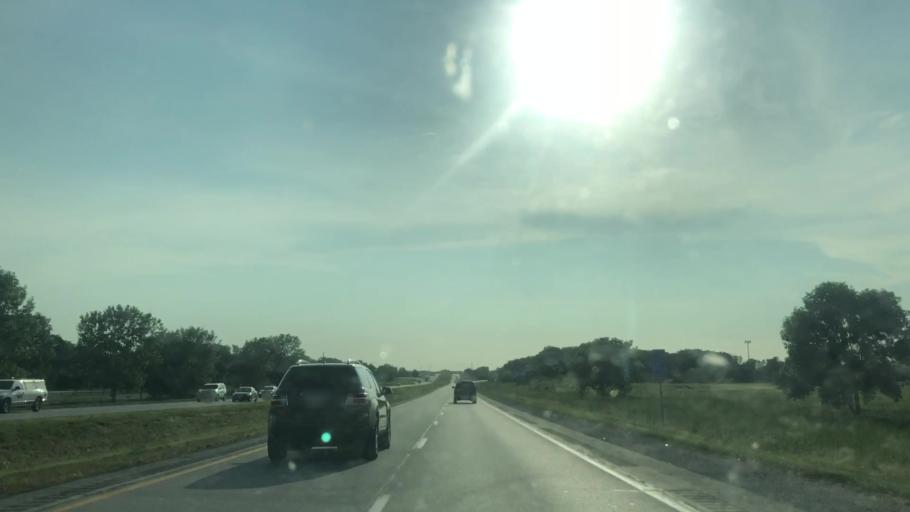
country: US
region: Iowa
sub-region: Story County
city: Ames
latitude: 42.0059
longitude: -93.5969
